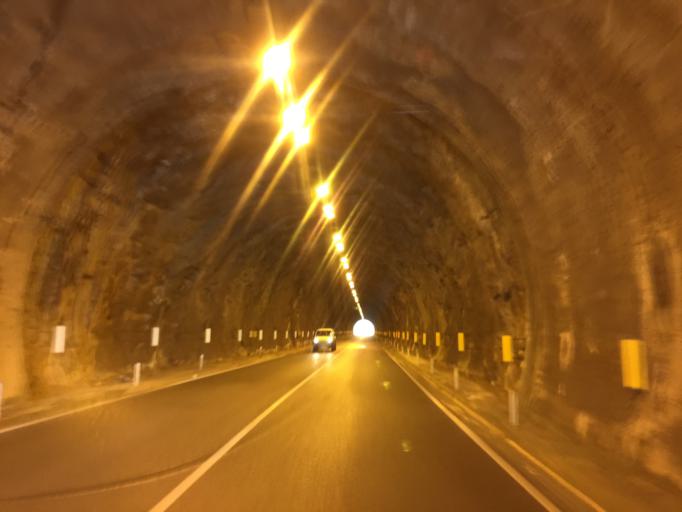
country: ES
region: Asturias
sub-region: Province of Asturias
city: Proaza
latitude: 43.2325
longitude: -6.0335
